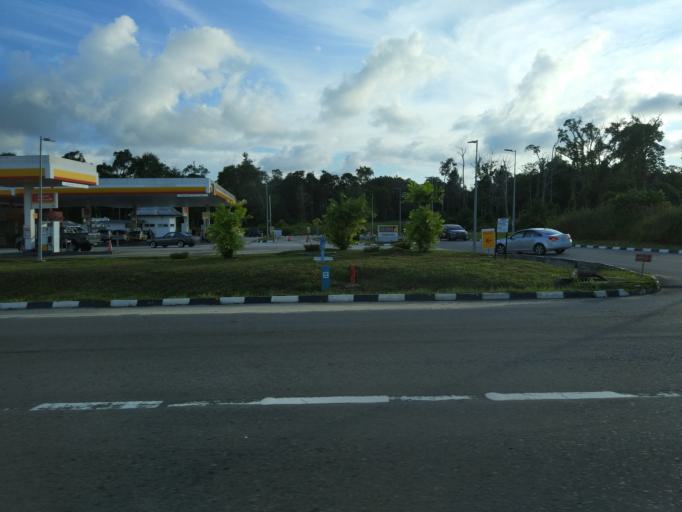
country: BN
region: Tutong
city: Tutong
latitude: 4.7788
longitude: 114.6537
